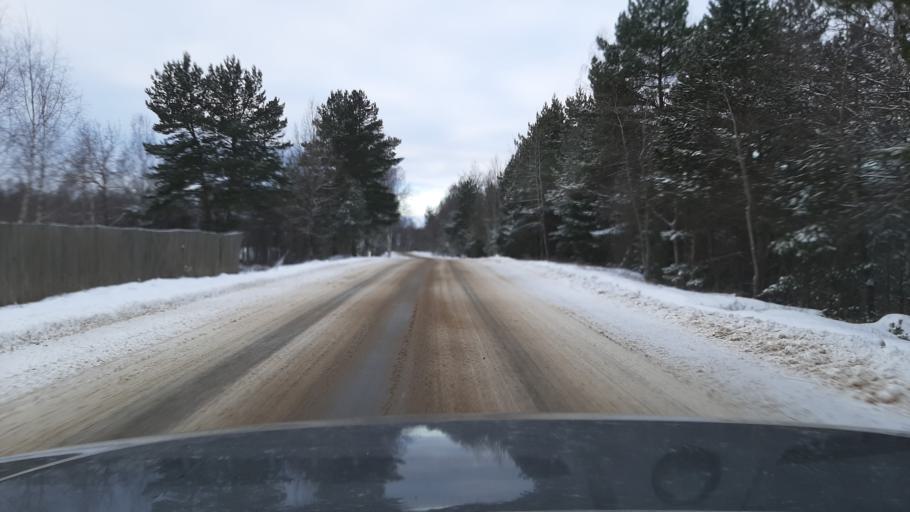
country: RU
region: Kostroma
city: Nerekhta
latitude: 57.4709
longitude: 40.6385
